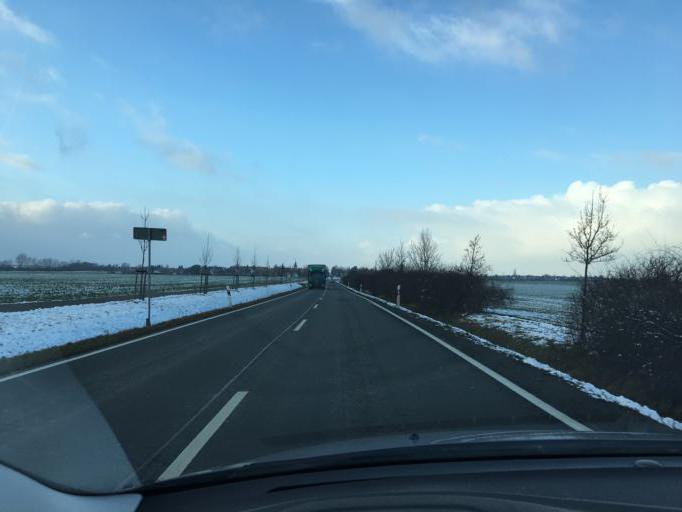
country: DE
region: Saxony
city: Brandis
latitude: 51.3461
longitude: 12.5959
